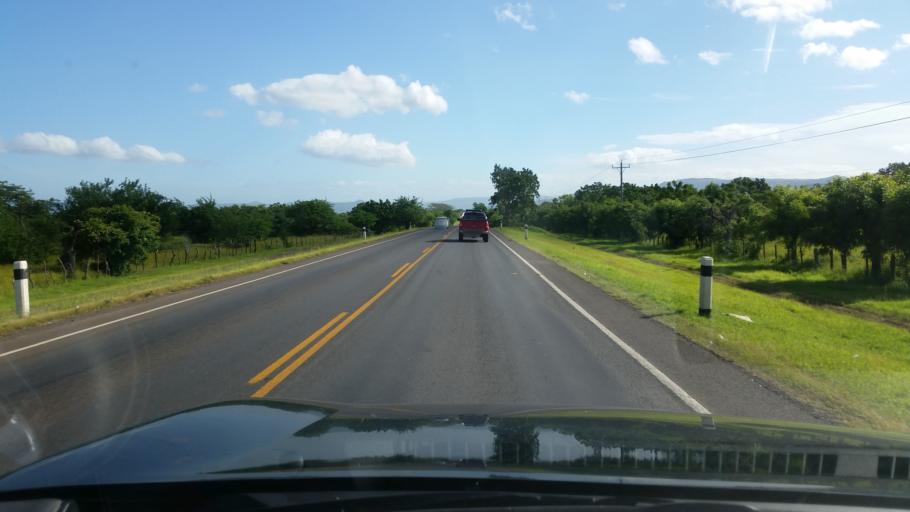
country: NI
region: Managua
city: Tipitapa
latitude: 12.3254
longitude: -86.0527
